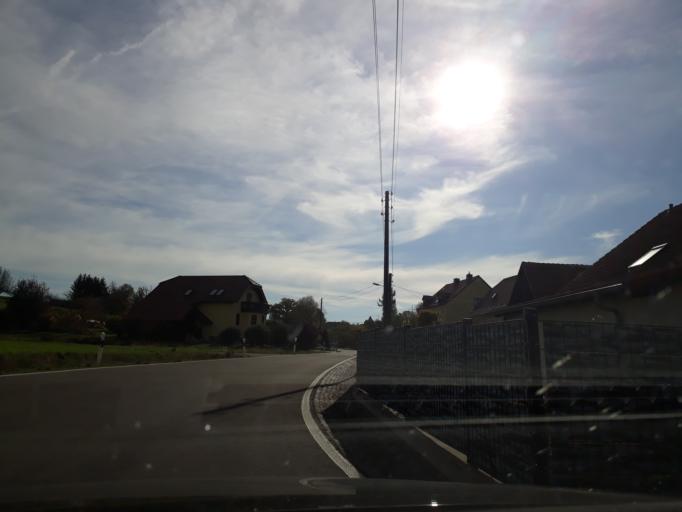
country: DE
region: Saxony
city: Niederstriegis
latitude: 51.1127
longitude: 13.1581
